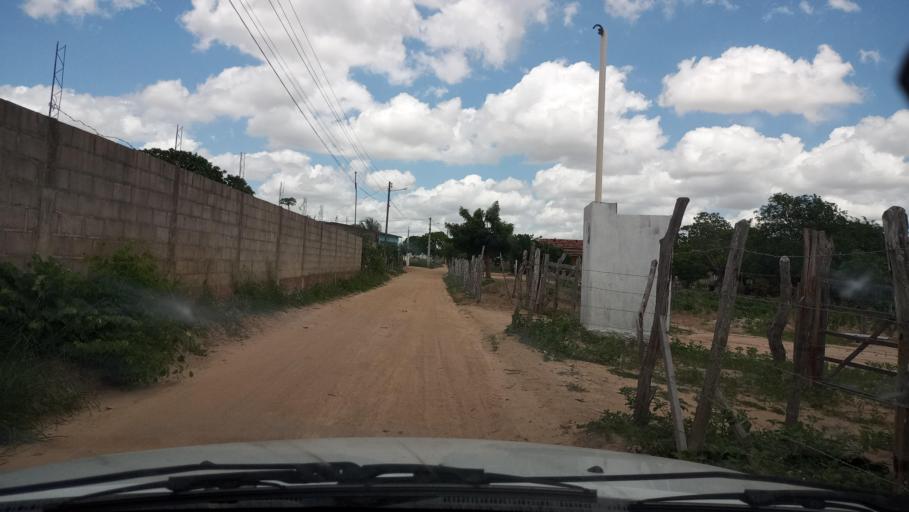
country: BR
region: Rio Grande do Norte
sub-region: Sao Jose Do Campestre
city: Sao Jose do Campestre
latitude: -6.4367
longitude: -35.6341
